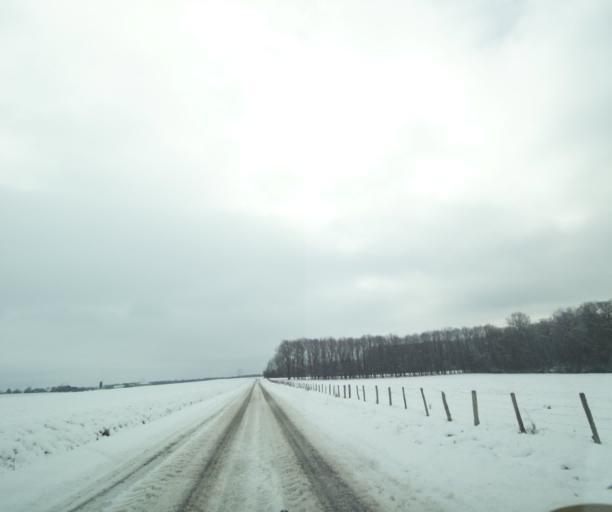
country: FR
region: Champagne-Ardenne
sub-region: Departement de la Haute-Marne
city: Montier-en-Der
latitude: 48.5182
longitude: 4.6790
